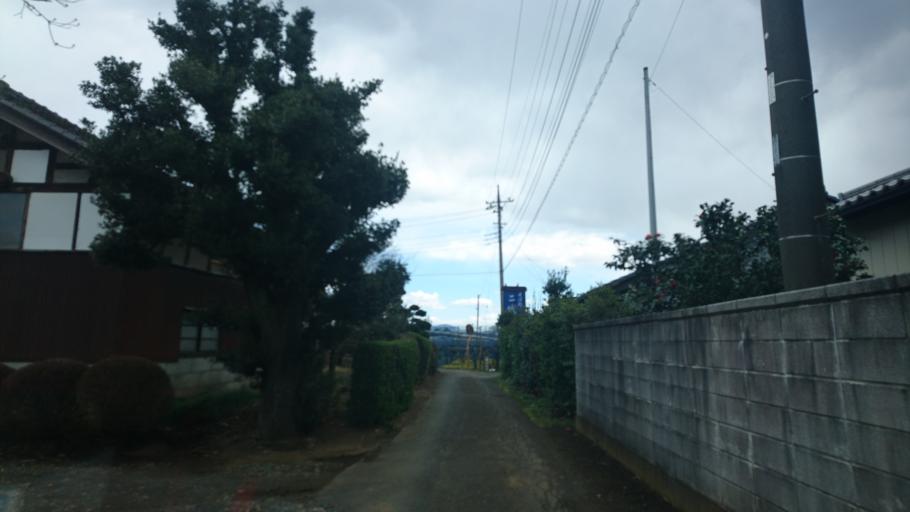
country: JP
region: Ibaraki
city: Yuki
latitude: 36.2631
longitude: 139.9147
